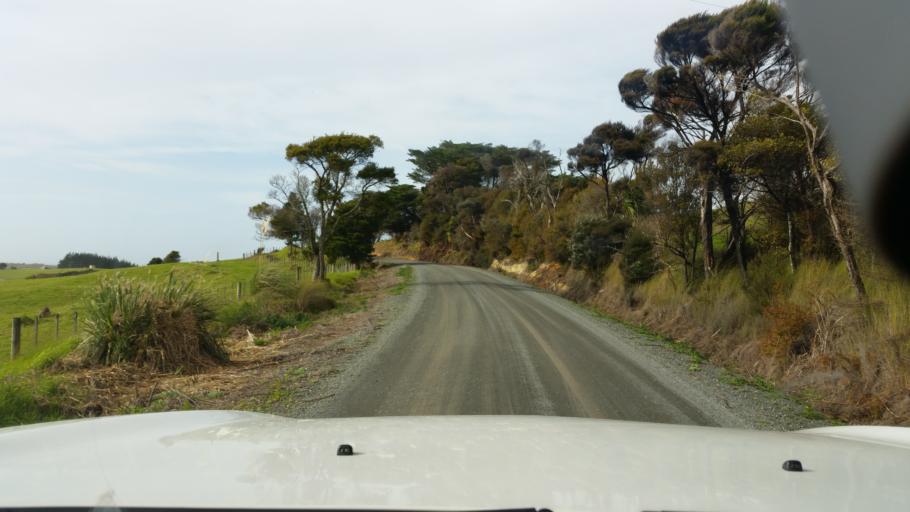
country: NZ
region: Northland
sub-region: Whangarei
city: Ruakaka
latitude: -35.7965
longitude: 174.5294
